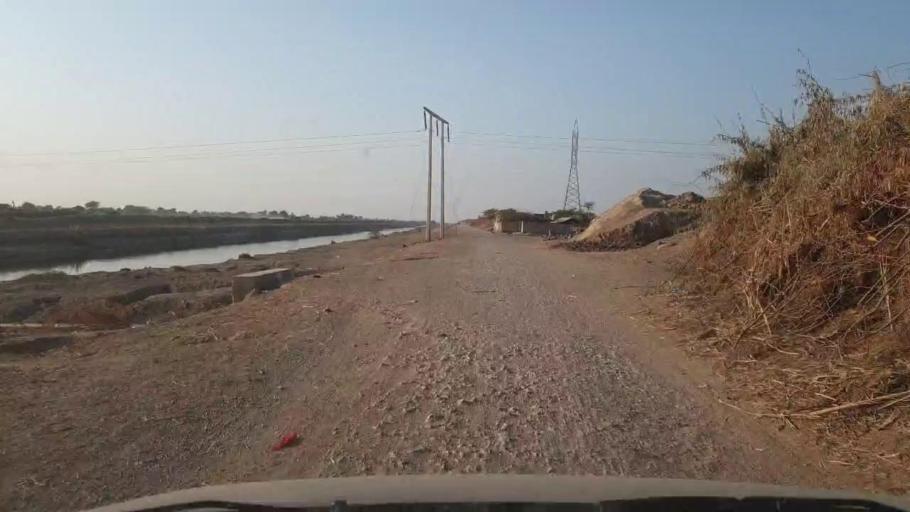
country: PK
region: Sindh
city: Samaro
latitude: 25.2797
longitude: 69.3415
